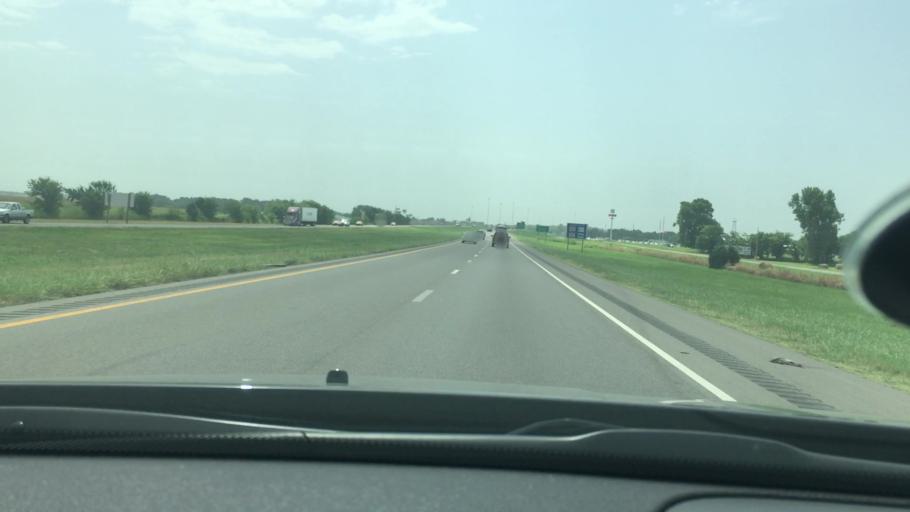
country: US
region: Oklahoma
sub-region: Garvin County
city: Pauls Valley
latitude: 34.7487
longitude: -97.2727
